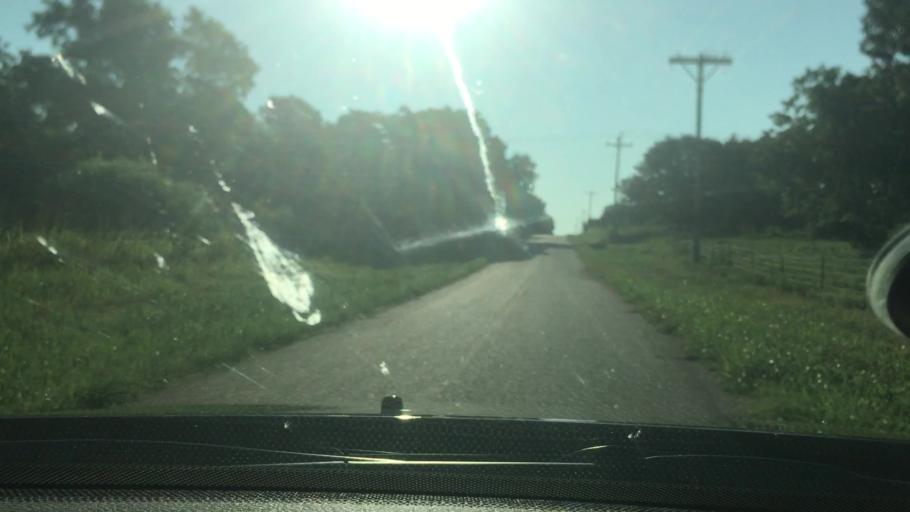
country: US
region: Oklahoma
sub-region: Murray County
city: Sulphur
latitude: 34.4049
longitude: -96.8119
